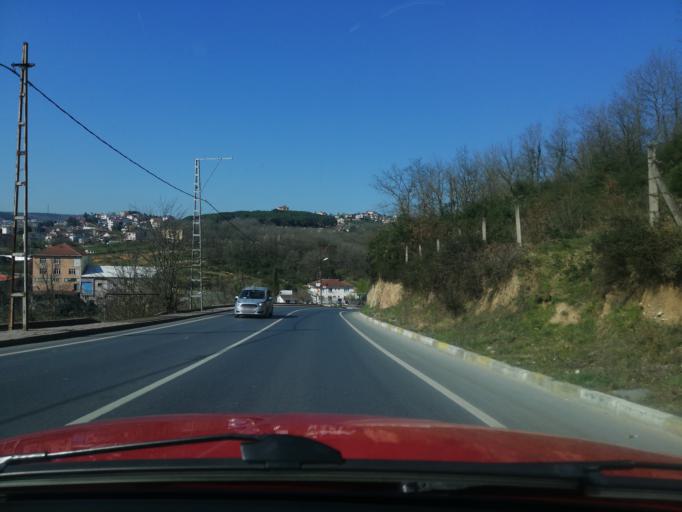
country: TR
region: Istanbul
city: Umraniye
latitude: 41.0775
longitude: 29.1446
